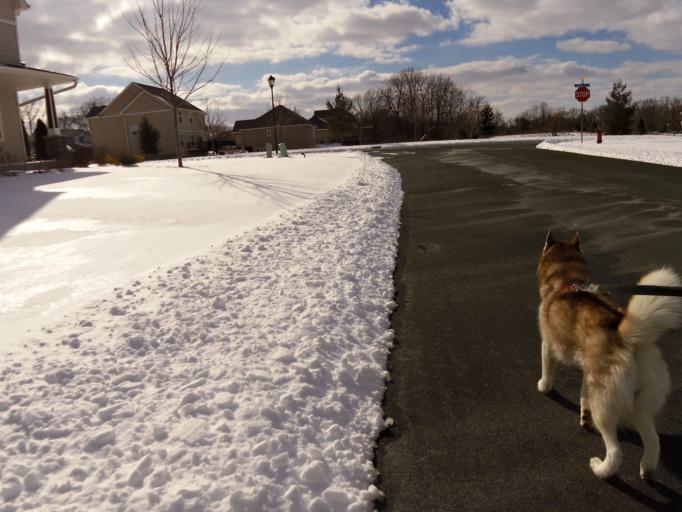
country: US
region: Minnesota
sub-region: Scott County
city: Prior Lake
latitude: 44.6933
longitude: -93.4519
